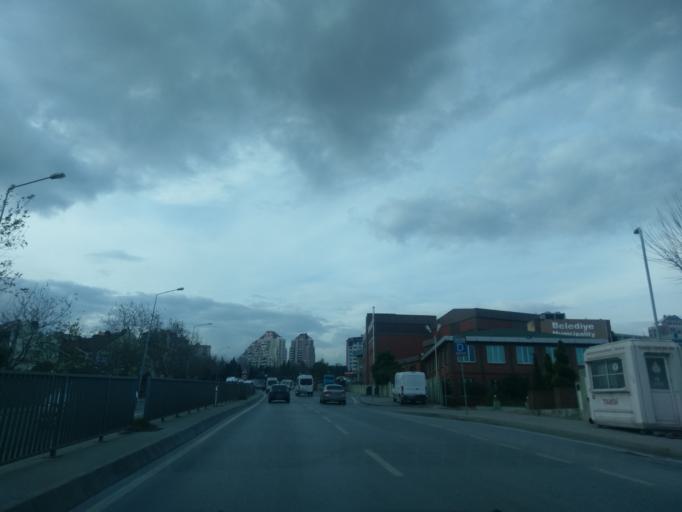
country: TR
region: Istanbul
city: Esenyurt
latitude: 41.0617
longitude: 28.6850
